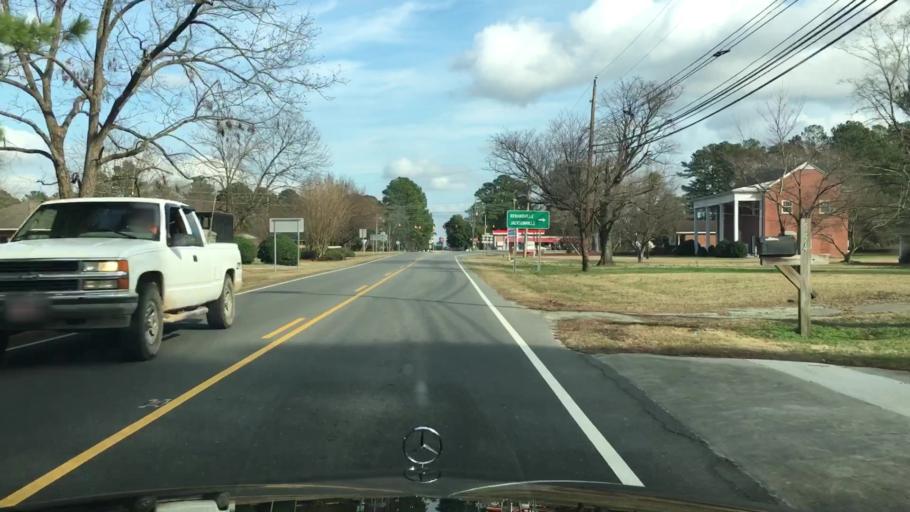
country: US
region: North Carolina
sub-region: Duplin County
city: Warsaw
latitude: 35.0018
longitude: -78.0822
